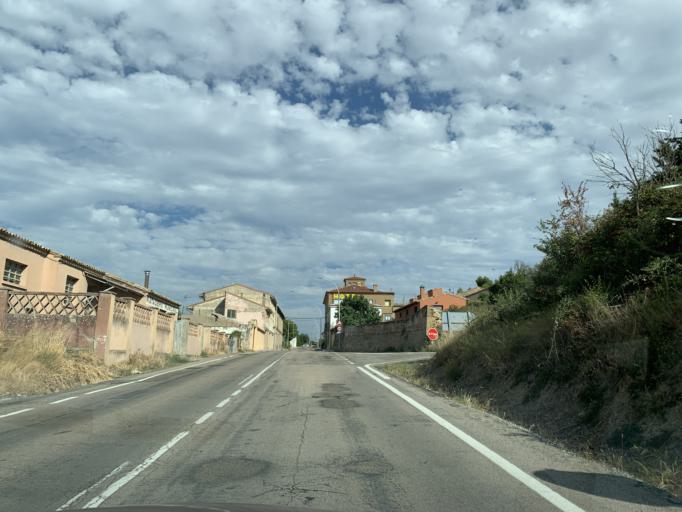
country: ES
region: Aragon
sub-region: Provincia de Huesca
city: Ayerbe
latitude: 42.2791
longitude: -0.6922
